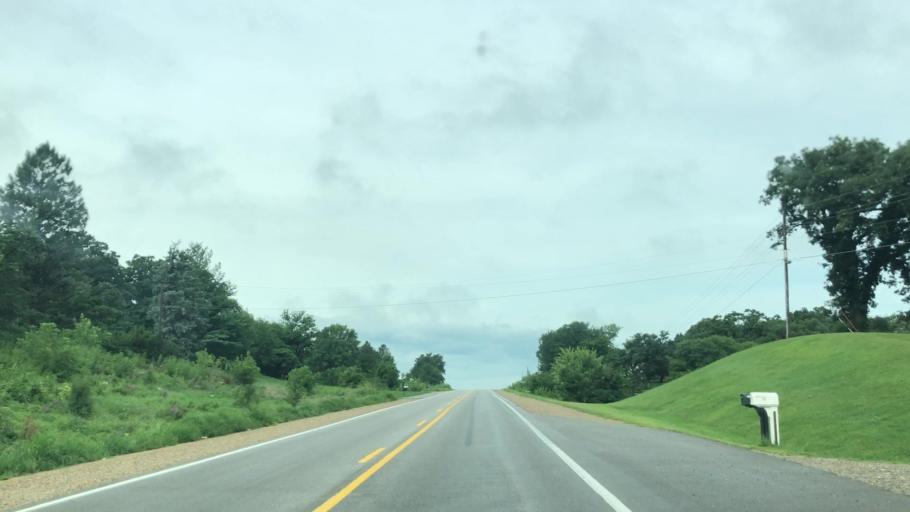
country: US
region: Iowa
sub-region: Marshall County
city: Marshalltown
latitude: 42.0076
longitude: -92.9469
